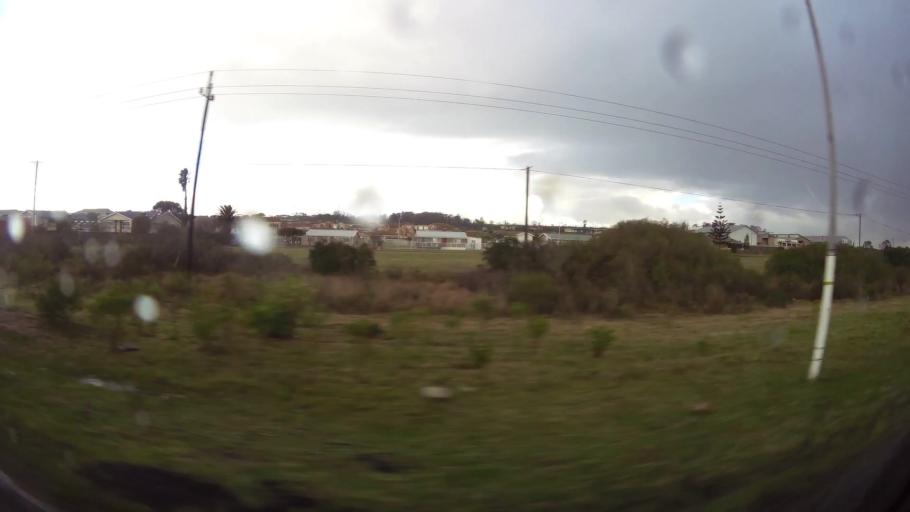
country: ZA
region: Western Cape
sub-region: Eden District Municipality
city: Mossel Bay
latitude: -34.1830
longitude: 22.0993
